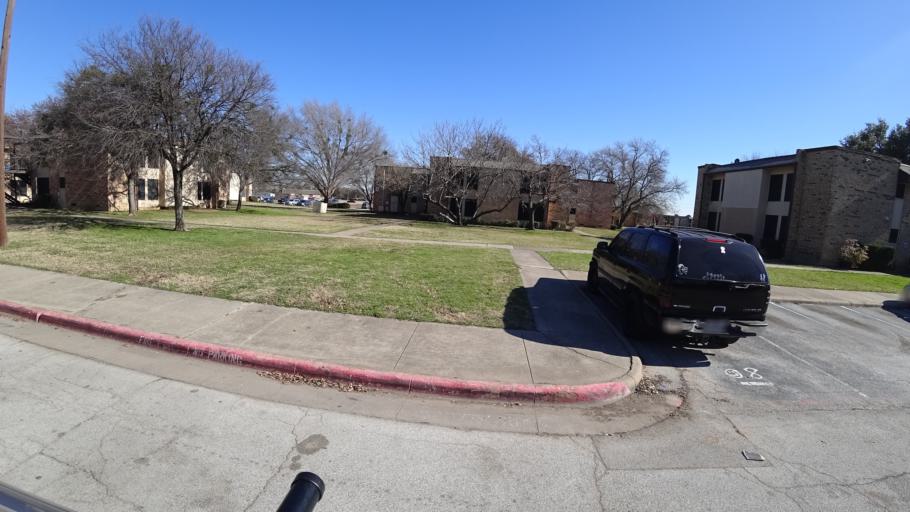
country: US
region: Texas
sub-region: Denton County
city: Lewisville
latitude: 33.0334
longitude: -97.0131
